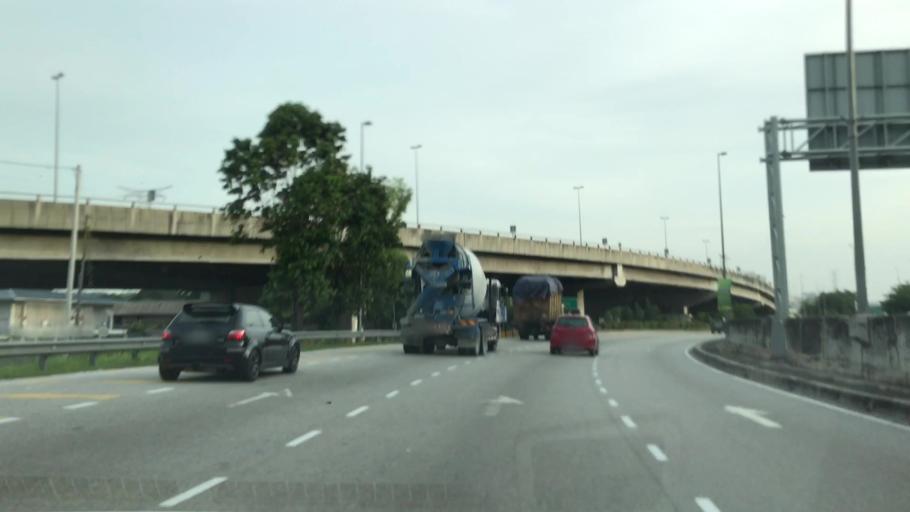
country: MY
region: Kuala Lumpur
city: Kuala Lumpur
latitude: 3.1053
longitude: 101.7066
